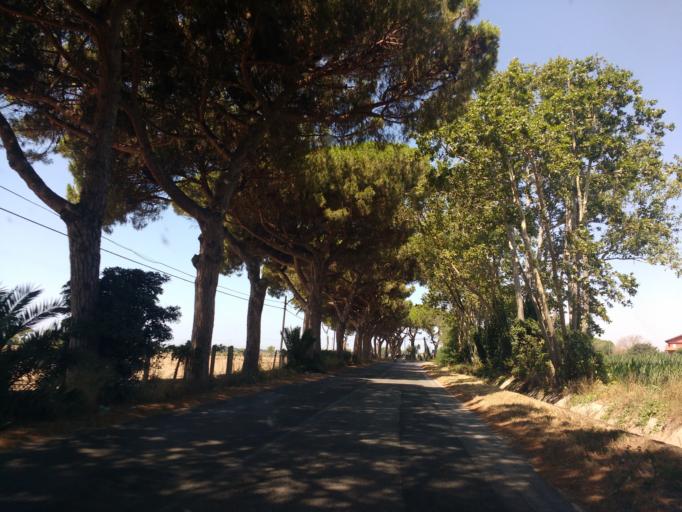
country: IT
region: Latium
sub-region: Citta metropolitana di Roma Capitale
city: Maccarese
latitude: 41.8808
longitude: 12.1971
